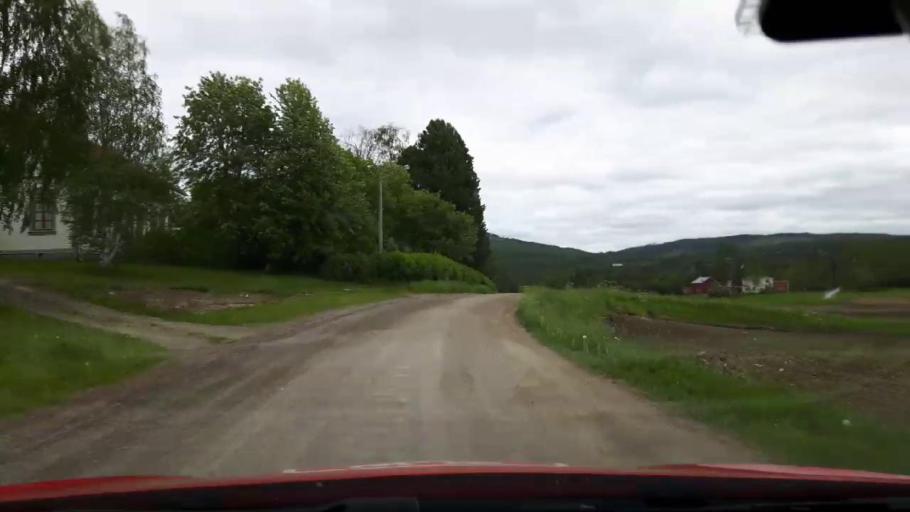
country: SE
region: Jaemtland
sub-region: Ragunda Kommun
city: Hammarstrand
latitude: 63.1573
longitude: 16.2373
